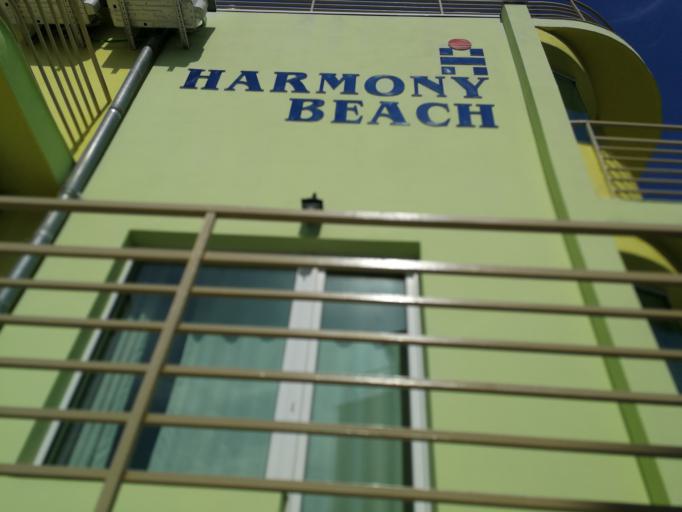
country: BG
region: Burgas
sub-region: Obshtina Nesebur
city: Ravda
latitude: 42.6518
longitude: 27.6914
